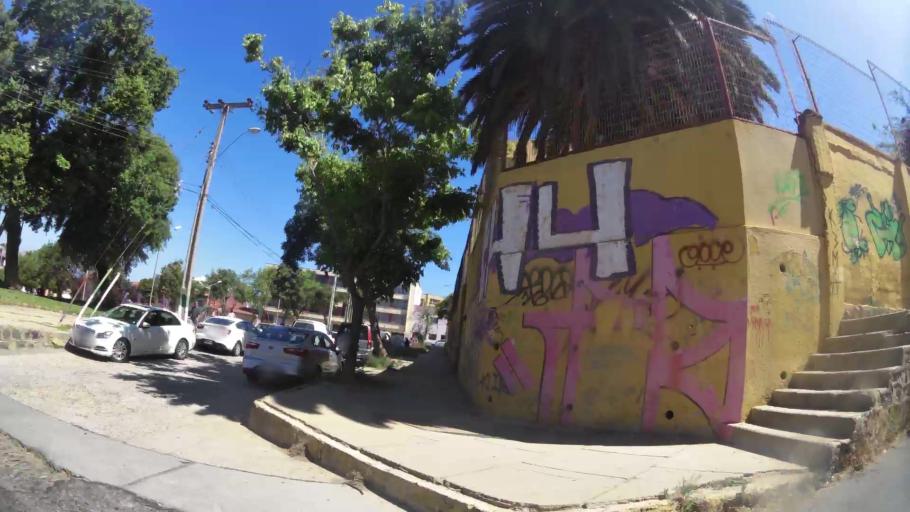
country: CL
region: Valparaiso
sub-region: Provincia de Valparaiso
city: Valparaiso
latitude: -33.0287
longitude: -71.6341
